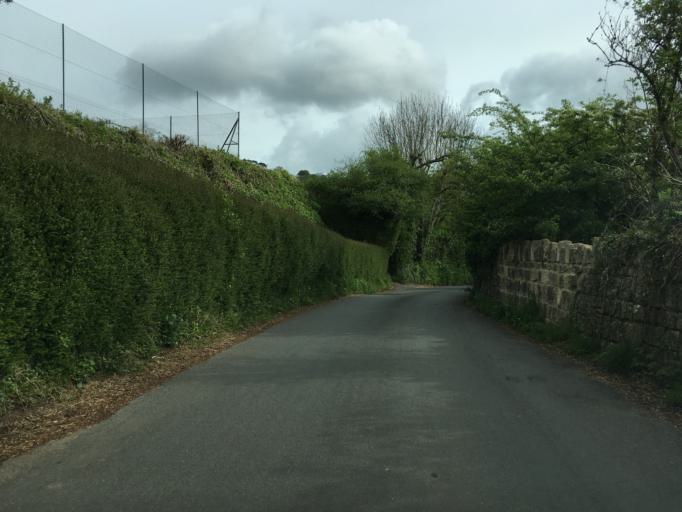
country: GB
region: England
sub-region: Bath and North East Somerset
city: Freshford
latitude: 51.3558
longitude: -2.3300
